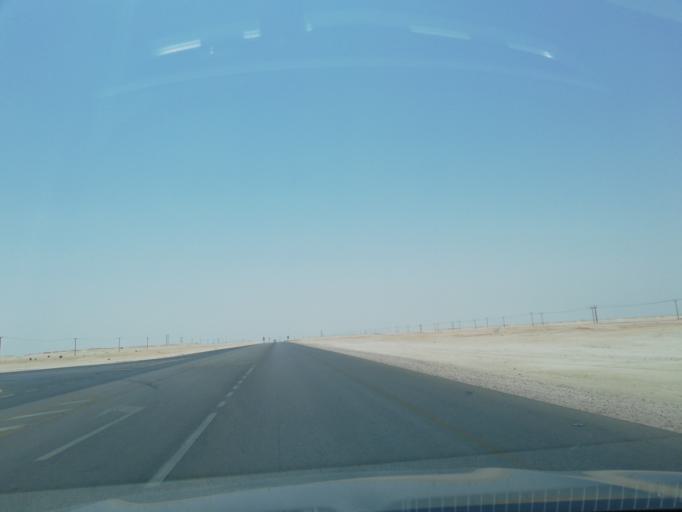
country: OM
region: Al Wusta
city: Hayma'
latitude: 19.9285
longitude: 56.2125
